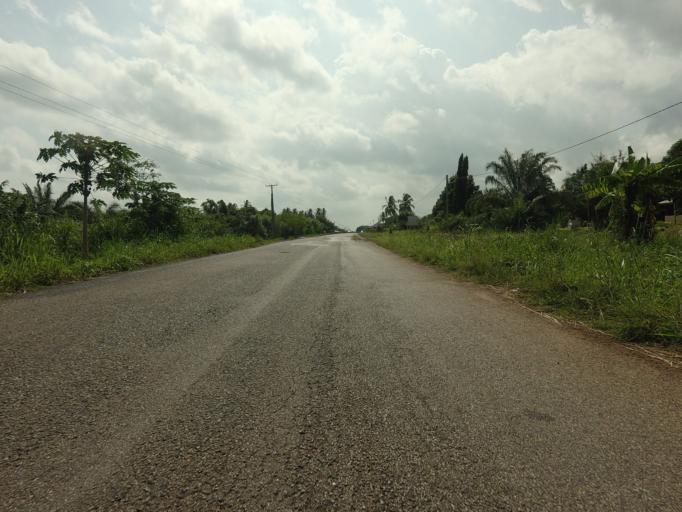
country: GH
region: Volta
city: Ho
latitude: 6.4123
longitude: 0.7594
